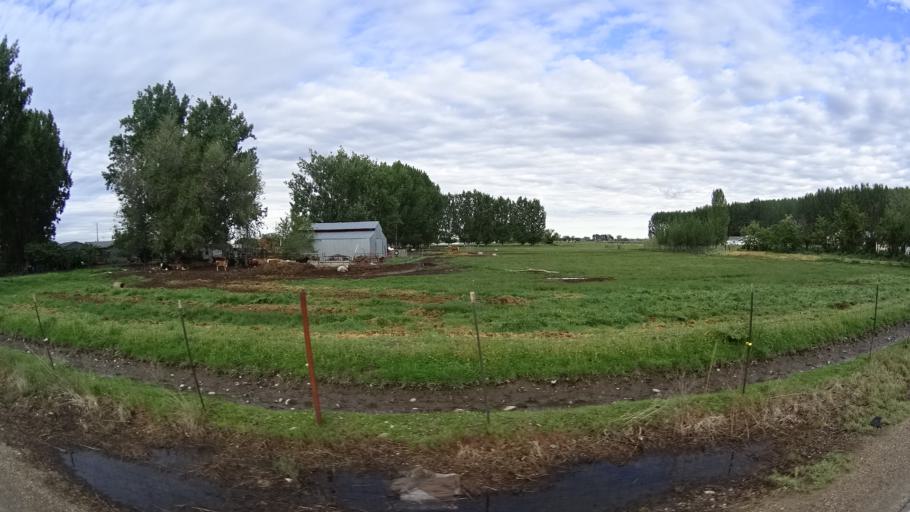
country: US
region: Idaho
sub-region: Ada County
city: Star
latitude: 43.6955
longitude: -116.5128
